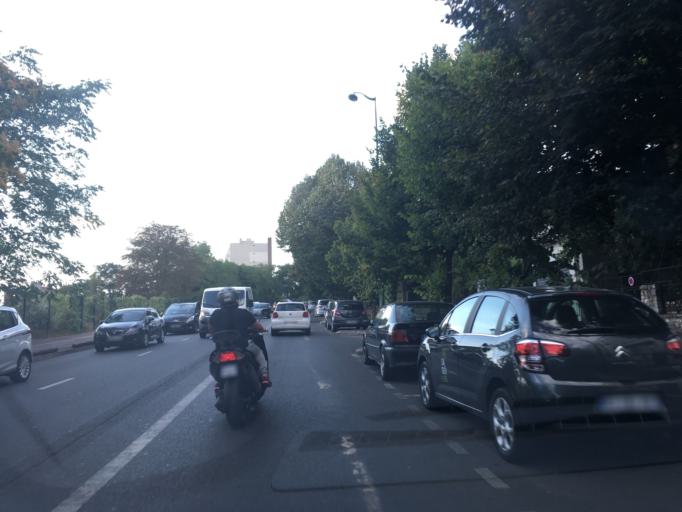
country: FR
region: Ile-de-France
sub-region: Departement du Val-de-Marne
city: Joinville-le-Pont
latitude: 48.8155
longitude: 2.4620
